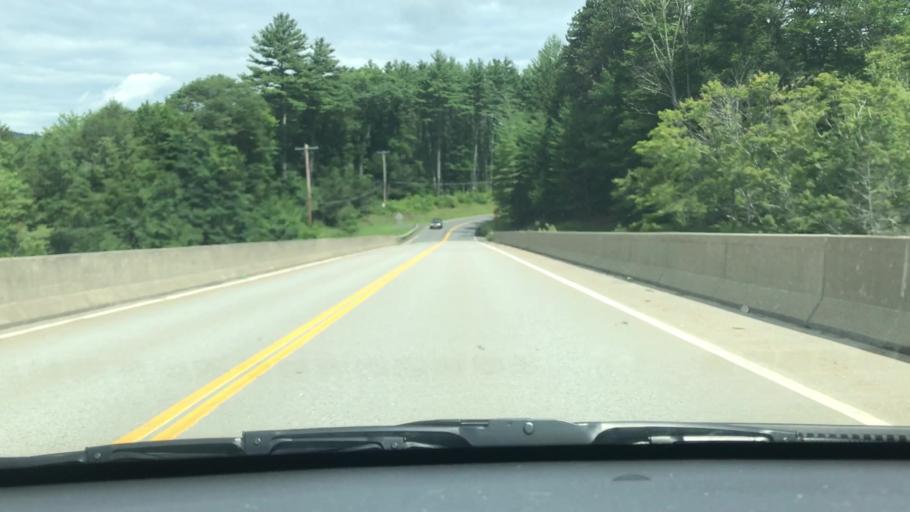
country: US
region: New York
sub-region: Ulster County
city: Shokan
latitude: 41.9921
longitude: -74.2778
